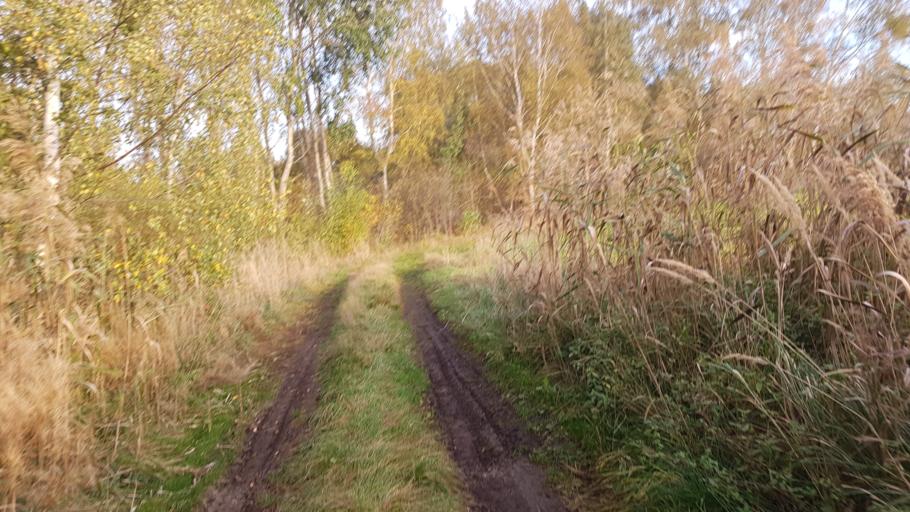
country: DE
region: Brandenburg
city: Schilda
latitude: 51.5666
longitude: 13.4059
